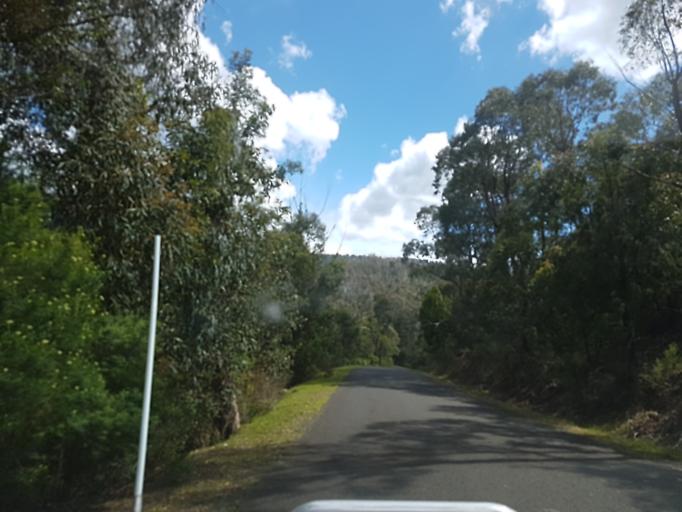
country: AU
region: Victoria
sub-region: East Gippsland
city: Bairnsdale
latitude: -37.4101
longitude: 147.2508
